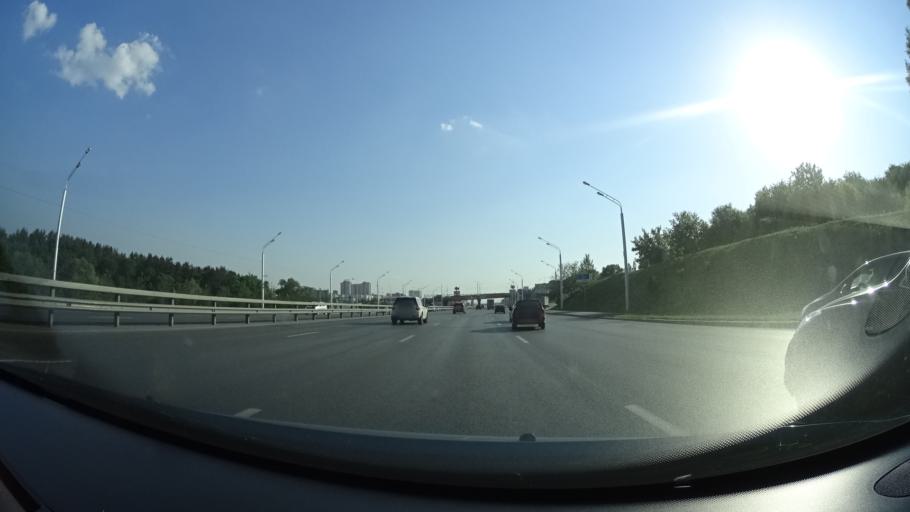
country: RU
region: Bashkortostan
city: Ufa
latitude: 54.7326
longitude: 56.0015
